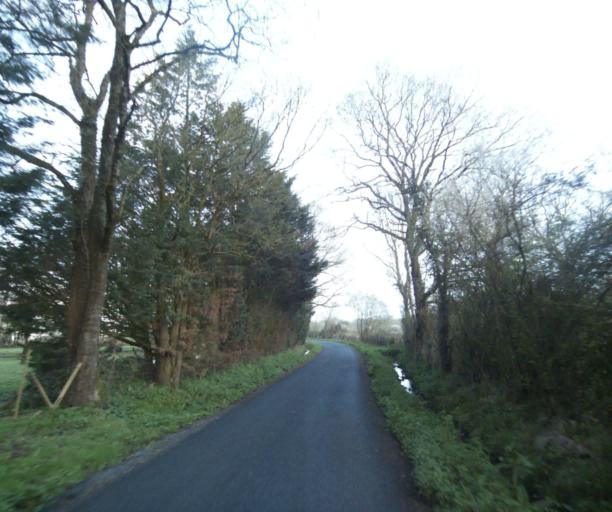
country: FR
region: Pays de la Loire
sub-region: Departement de la Loire-Atlantique
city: Savenay
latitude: 47.3905
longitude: -1.9106
